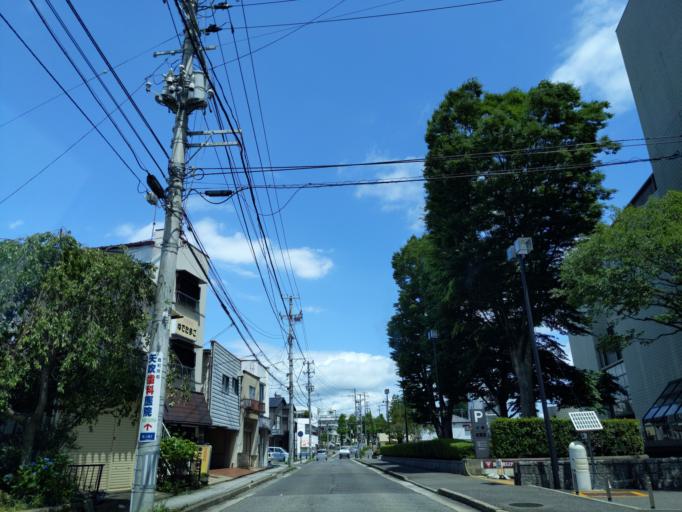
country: JP
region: Fukushima
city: Koriyama
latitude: 37.3922
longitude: 140.3775
